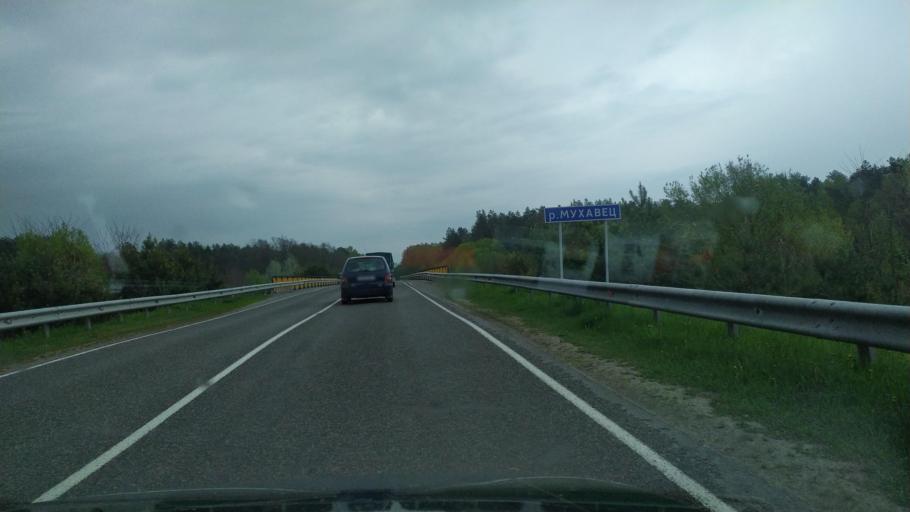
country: BY
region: Brest
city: Horad Kobryn
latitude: 52.2987
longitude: 24.5164
